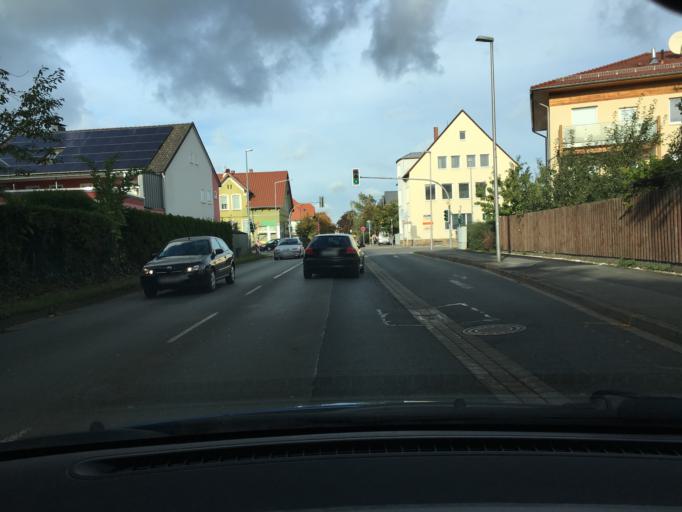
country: DE
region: Lower Saxony
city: Barsinghausen
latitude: 52.3038
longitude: 9.4669
